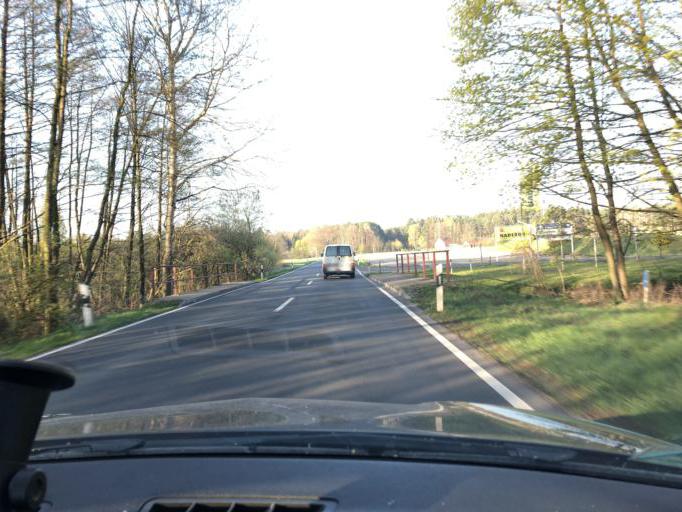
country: DE
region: Saxony
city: Krauschwitz
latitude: 51.5092
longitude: 14.7177
